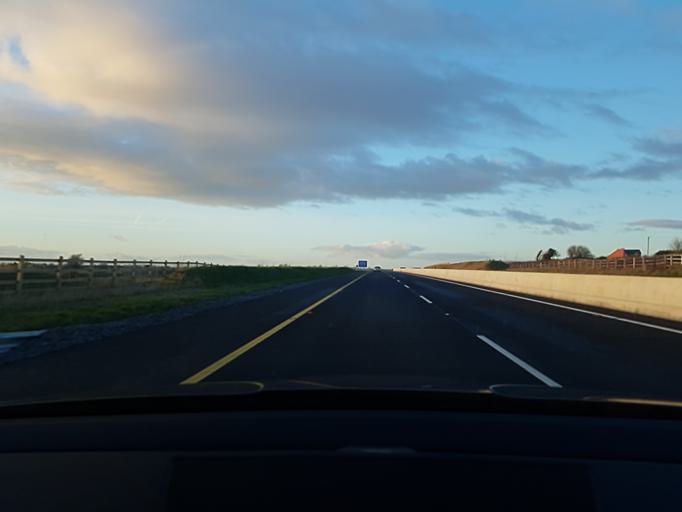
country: IE
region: Connaught
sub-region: County Galway
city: Athenry
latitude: 53.3812
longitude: -8.7983
